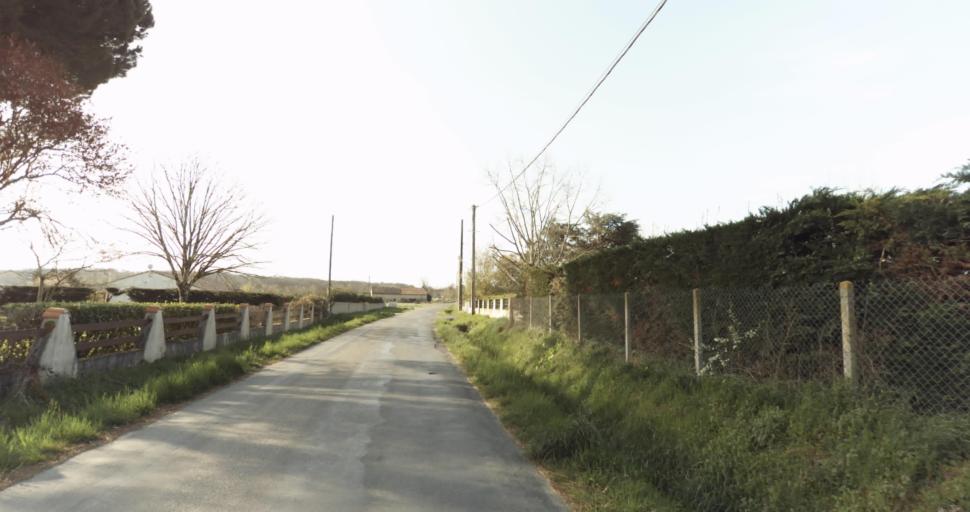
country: FR
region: Midi-Pyrenees
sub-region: Departement du Tarn
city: Saint-Sulpice-la-Pointe
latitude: 43.7577
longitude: 1.6772
